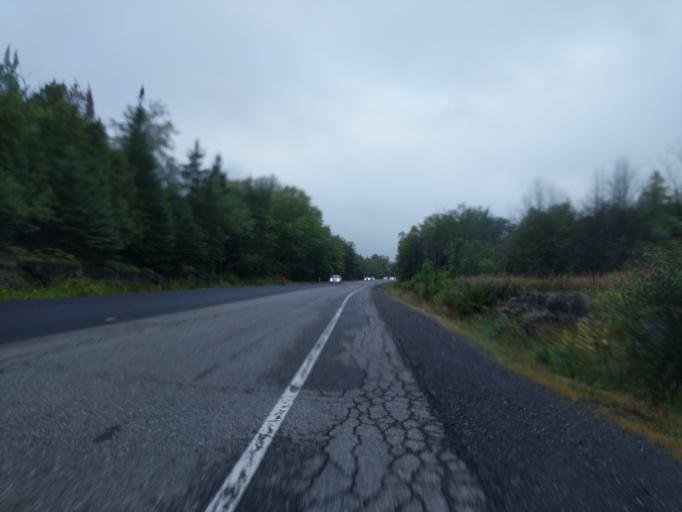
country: CA
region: Ontario
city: Bells Corners
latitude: 45.3197
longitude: -75.8549
